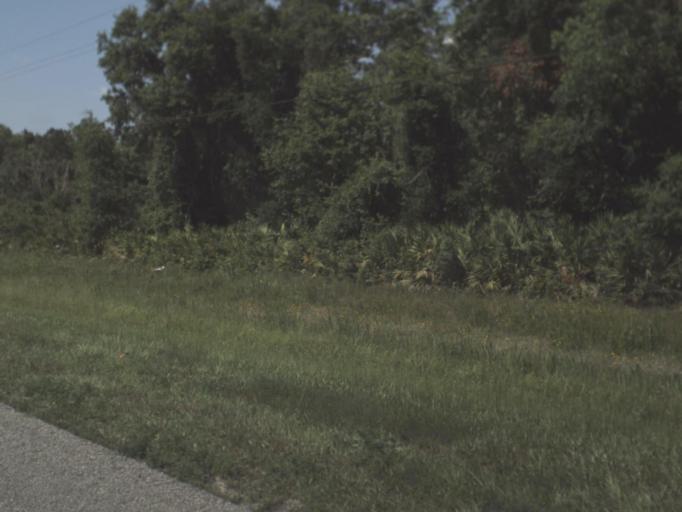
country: US
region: Florida
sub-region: Alachua County
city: Hawthorne
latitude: 29.5153
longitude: -82.1015
